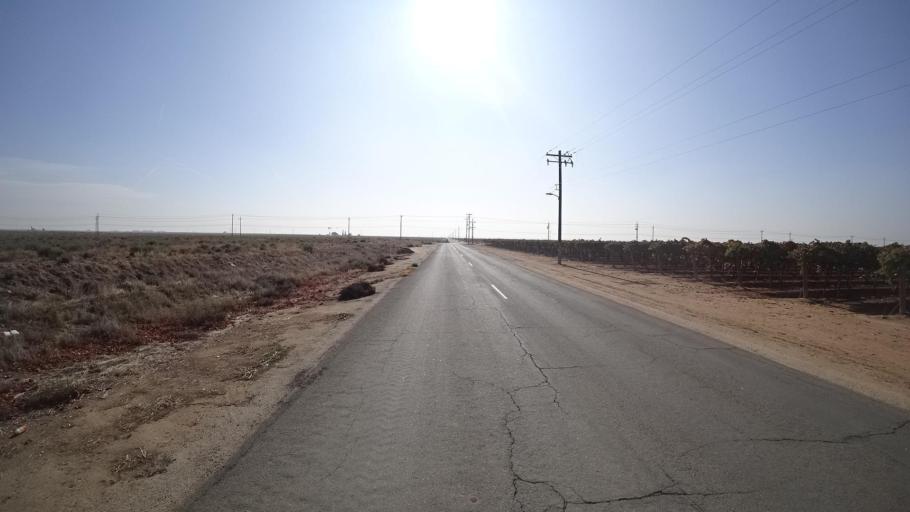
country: US
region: California
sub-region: Kern County
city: Greenacres
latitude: 35.5008
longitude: -119.1164
